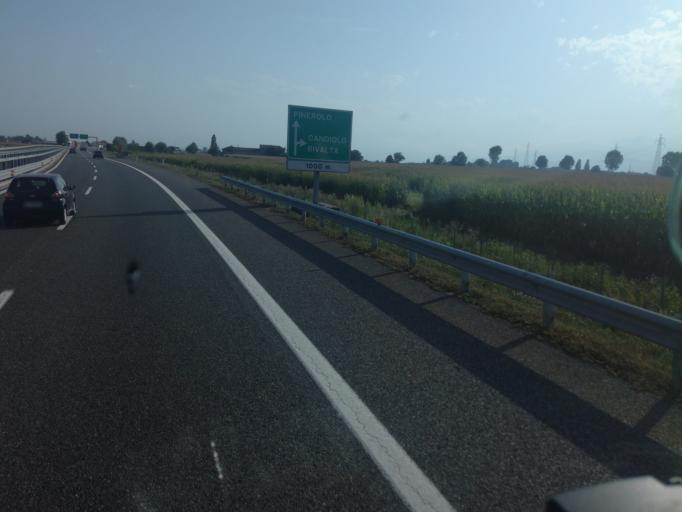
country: IT
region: Piedmont
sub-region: Provincia di Torino
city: Pasta
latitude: 44.9926
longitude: 7.5606
